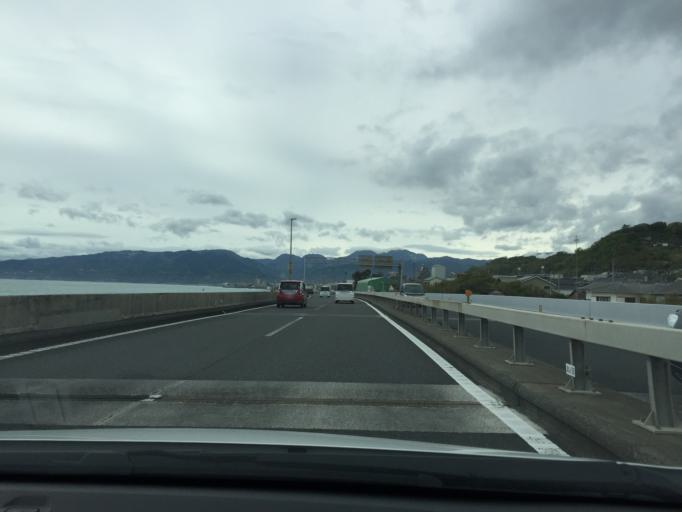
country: JP
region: Kanagawa
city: Ninomiya
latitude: 35.2836
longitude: 139.2262
